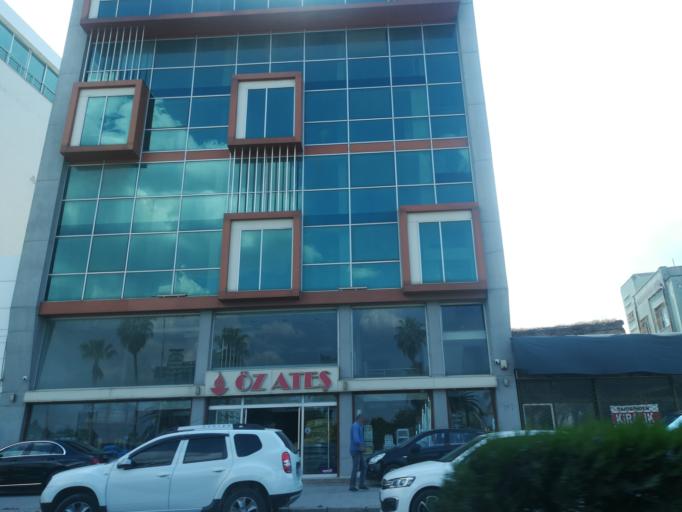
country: TR
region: Adana
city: Adana
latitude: 36.9874
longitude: 35.3322
